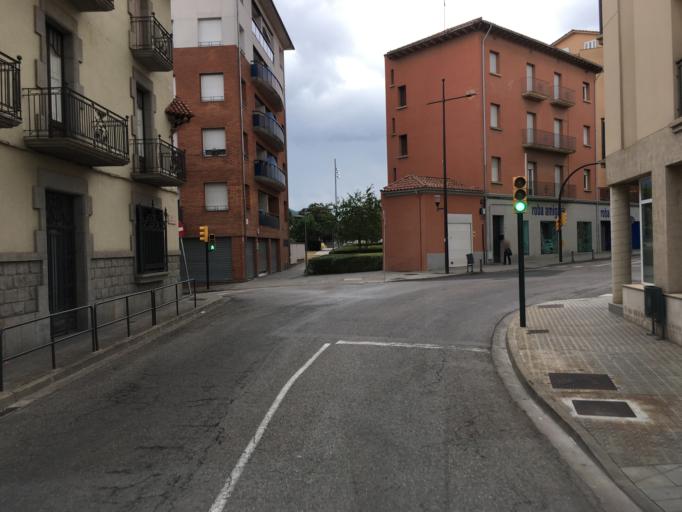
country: ES
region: Catalonia
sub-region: Provincia de Girona
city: Olot
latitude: 42.1817
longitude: 2.4925
